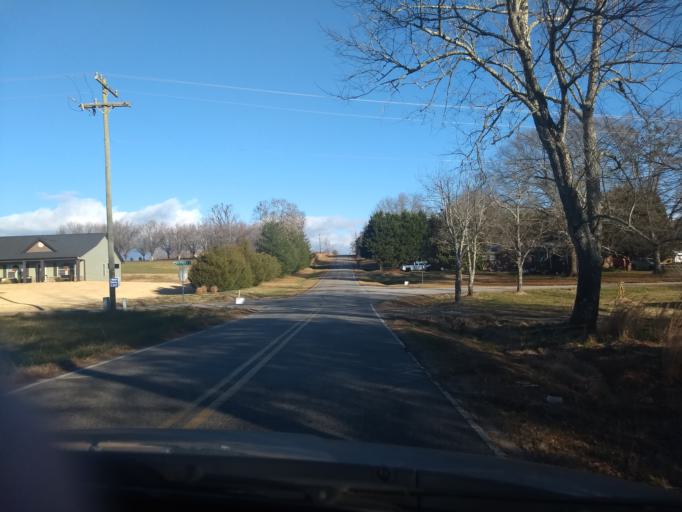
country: US
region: South Carolina
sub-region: Greenville County
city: Greer
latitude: 35.0263
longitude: -82.2016
